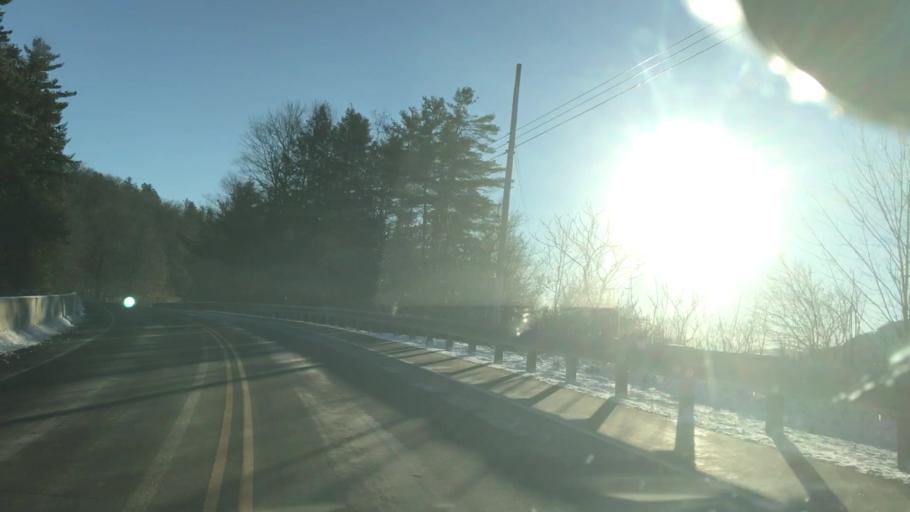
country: US
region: New Hampshire
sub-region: Grafton County
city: Orford
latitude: 43.9560
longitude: -72.0983
